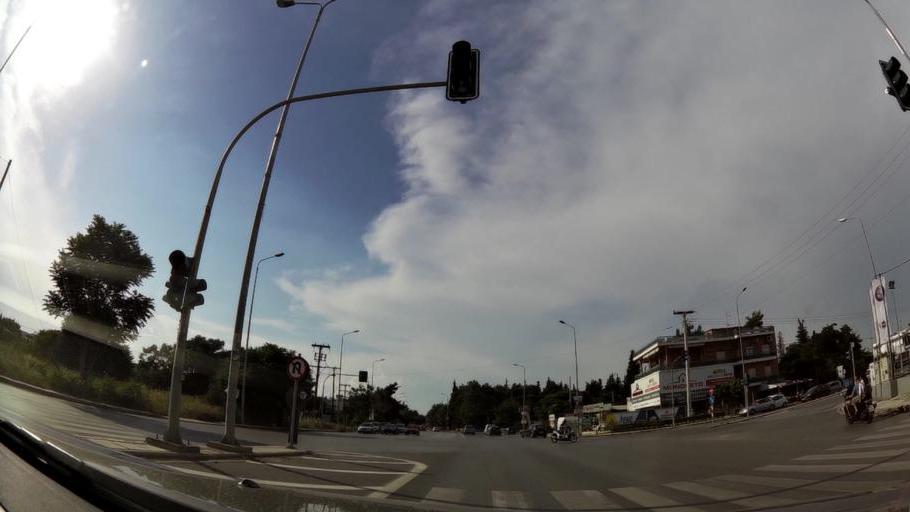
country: GR
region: Central Macedonia
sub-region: Nomos Thessalonikis
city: Kalamaria
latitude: 40.5674
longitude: 22.9747
